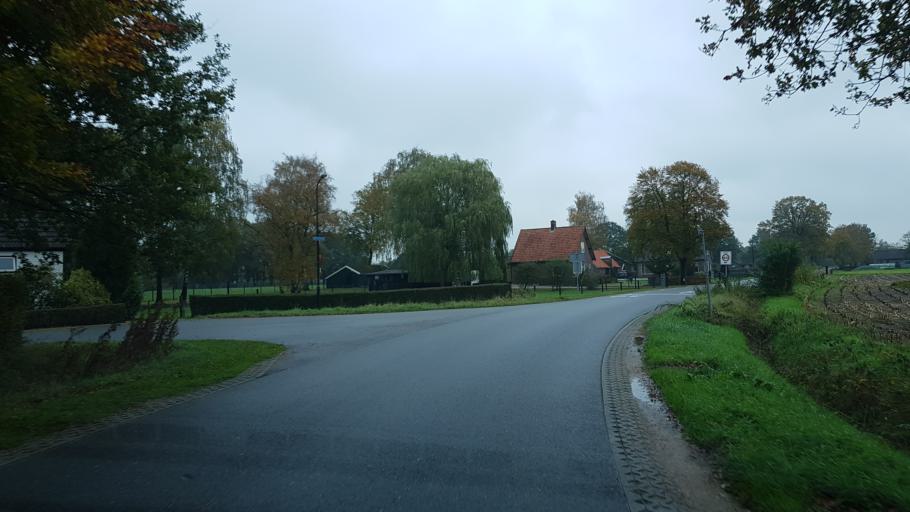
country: NL
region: Gelderland
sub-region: Gemeente Epe
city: Vaassen
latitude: 52.2560
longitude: 5.9682
